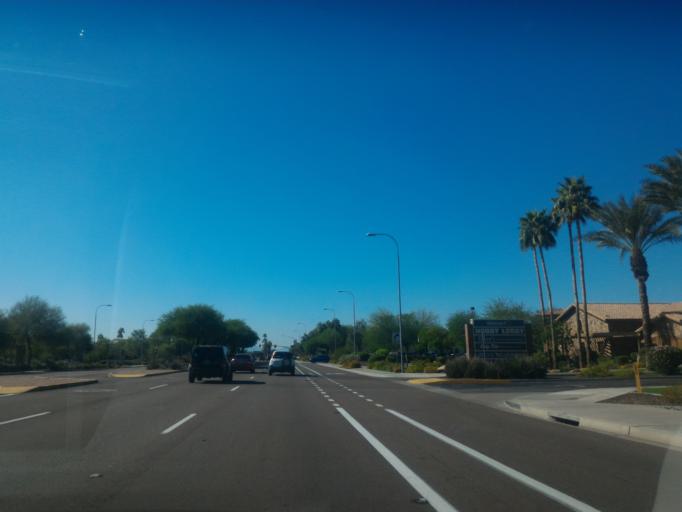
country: US
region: Arizona
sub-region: Maricopa County
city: Chandler
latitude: 33.3059
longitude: -111.9001
